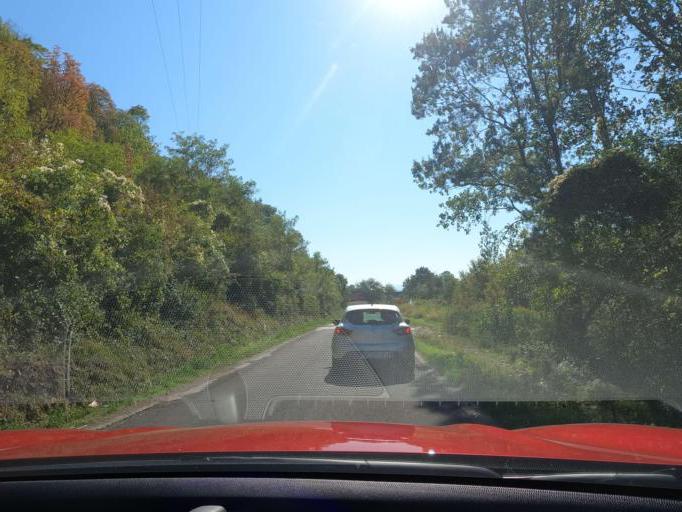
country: RS
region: Central Serbia
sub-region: Raski Okrug
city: Kraljevo
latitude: 43.7334
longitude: 20.7428
